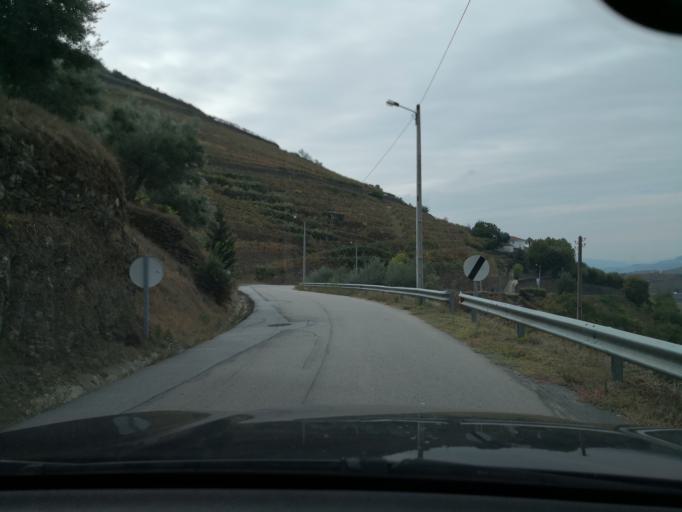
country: PT
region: Vila Real
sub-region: Peso da Regua
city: Peso da Regua
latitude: 41.1869
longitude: -7.7374
